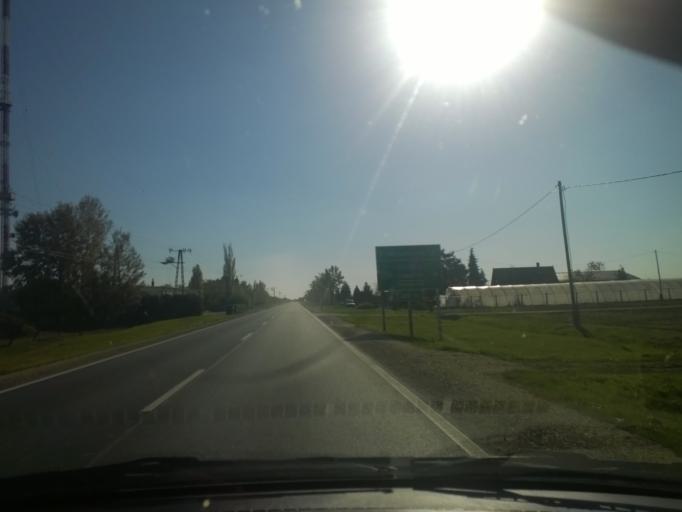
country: HU
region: Csongrad
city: Szentes
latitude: 46.6258
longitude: 20.2785
